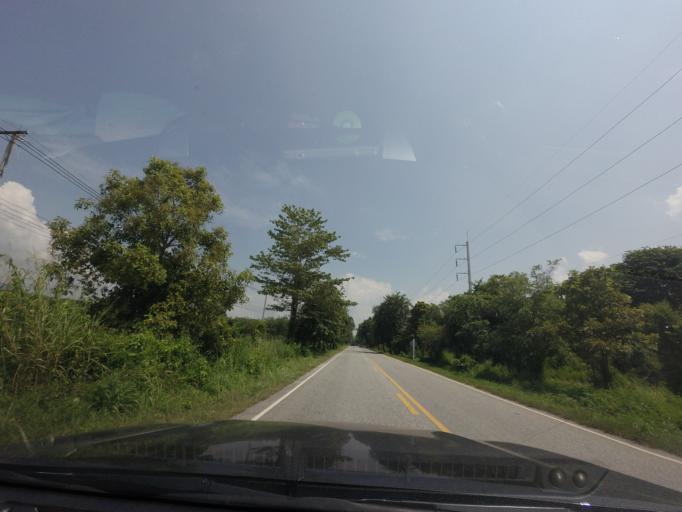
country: TH
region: Uttaradit
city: Thong Saen Khan
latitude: 17.4619
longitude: 100.2936
